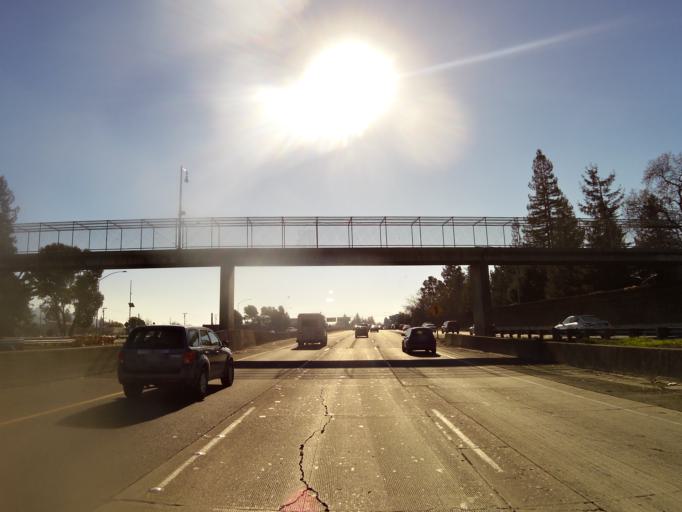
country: US
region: California
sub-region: Sonoma County
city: Santa Rosa
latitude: 38.4300
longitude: -122.7152
